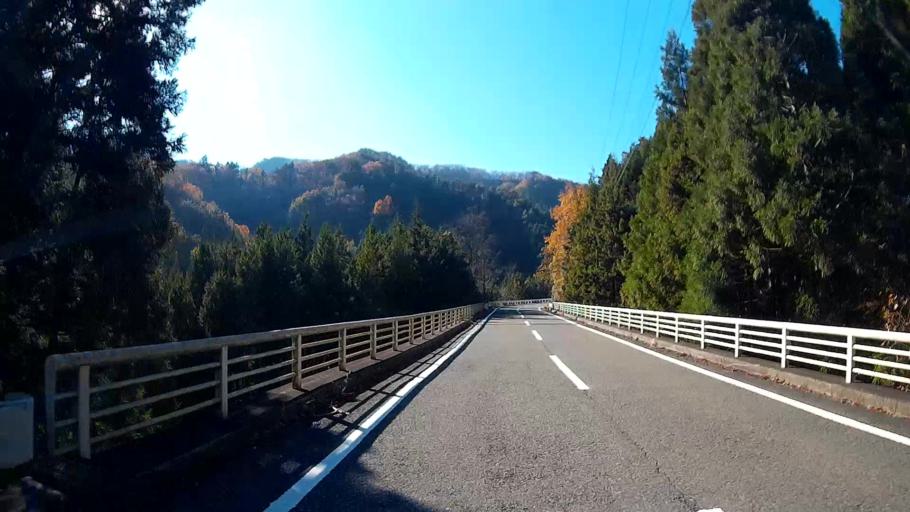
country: JP
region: Yamanashi
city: Otsuki
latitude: 35.5706
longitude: 139.0176
